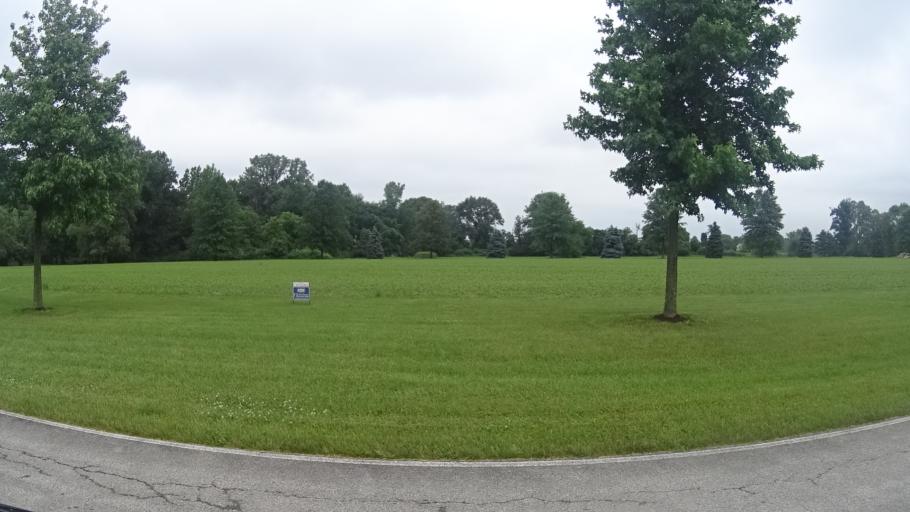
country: US
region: Ohio
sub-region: Erie County
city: Milan
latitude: 41.3032
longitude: -82.5458
